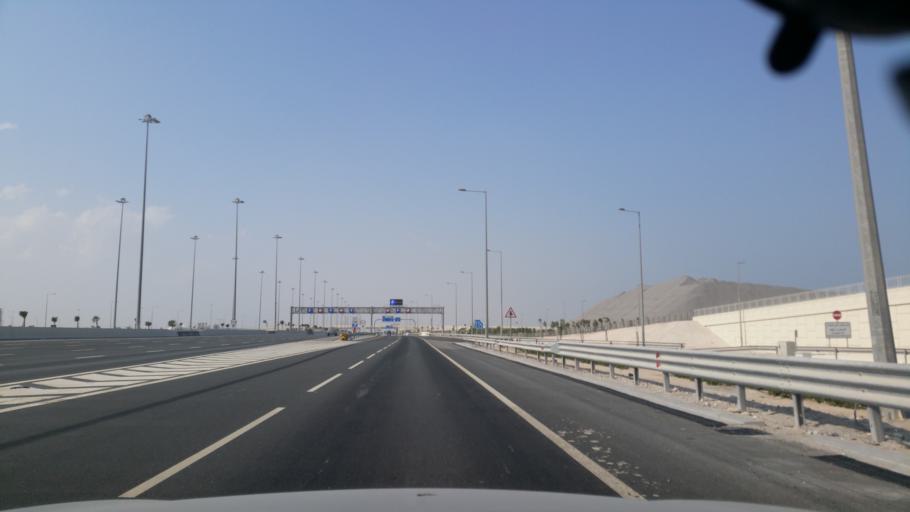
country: QA
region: Baladiyat Umm Salal
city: Umm Salal Muhammad
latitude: 25.4487
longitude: 51.4804
